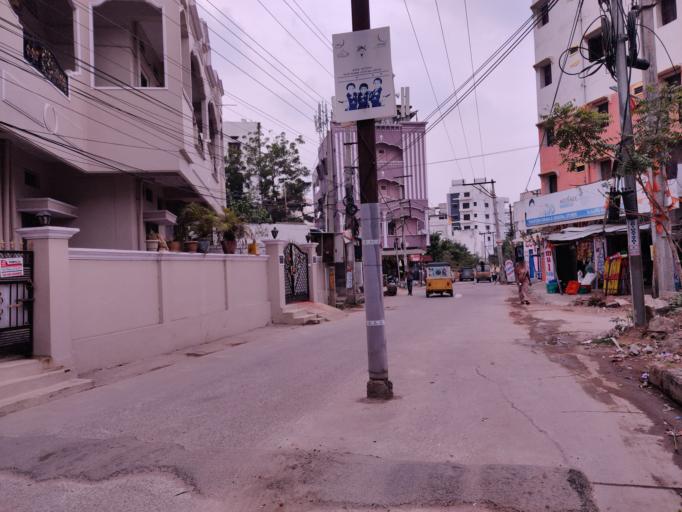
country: IN
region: Telangana
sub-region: Hyderabad
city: Hyderabad
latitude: 17.4064
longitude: 78.3977
